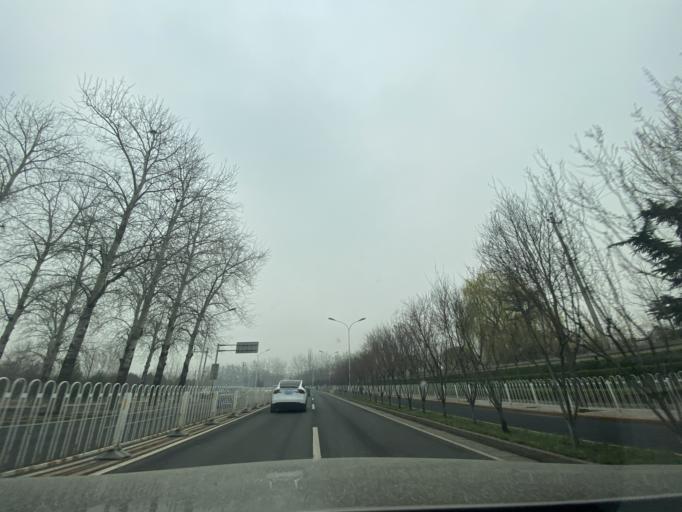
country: CN
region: Beijing
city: Sijiqing
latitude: 39.9699
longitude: 116.2584
